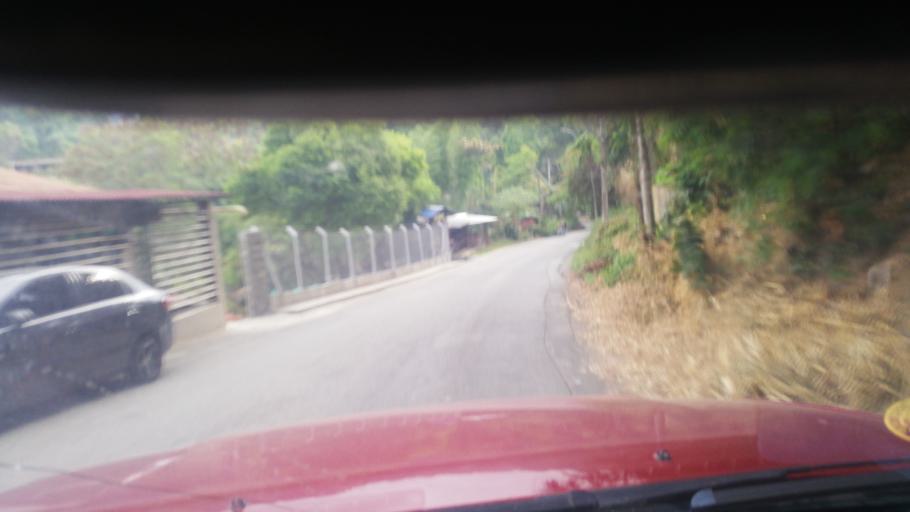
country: CO
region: Valle del Cauca
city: Cali
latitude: 3.4817
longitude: -76.5526
